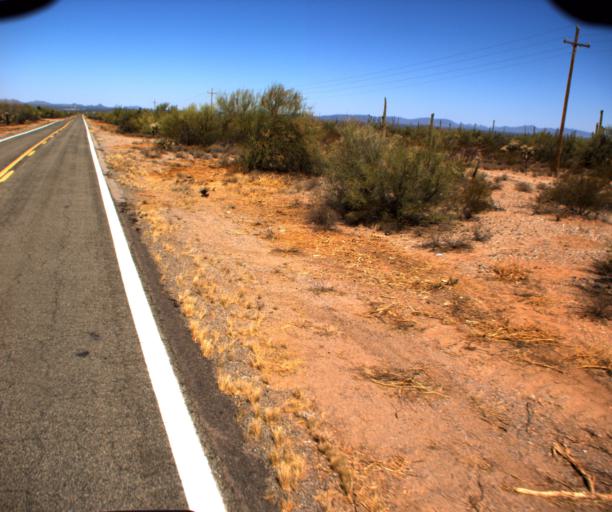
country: US
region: Arizona
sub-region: Pima County
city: Sells
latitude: 32.1820
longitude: -112.2822
